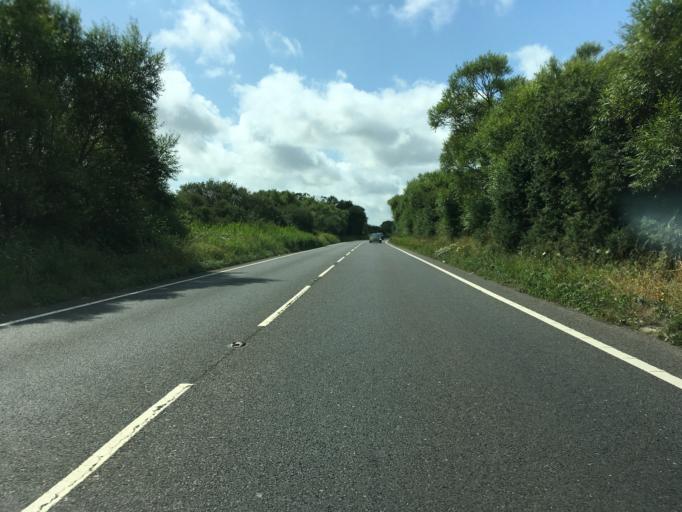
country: GB
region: England
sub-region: East Sussex
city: Pevensey
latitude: 50.8254
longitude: 0.3503
